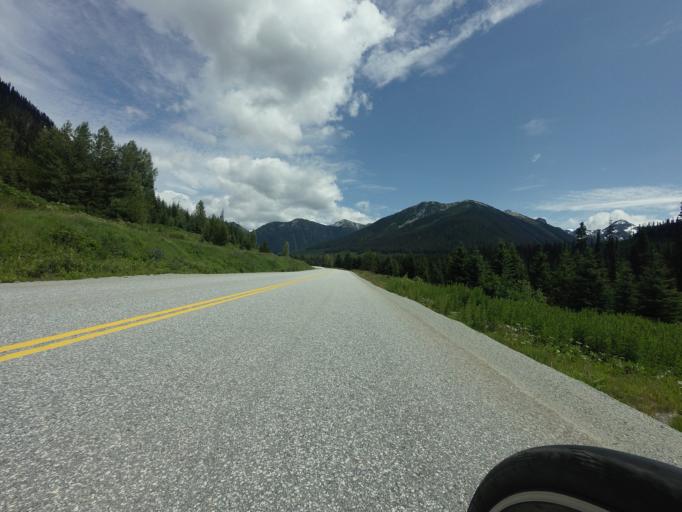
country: CA
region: British Columbia
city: Pemberton
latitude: 50.3828
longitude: -122.4240
